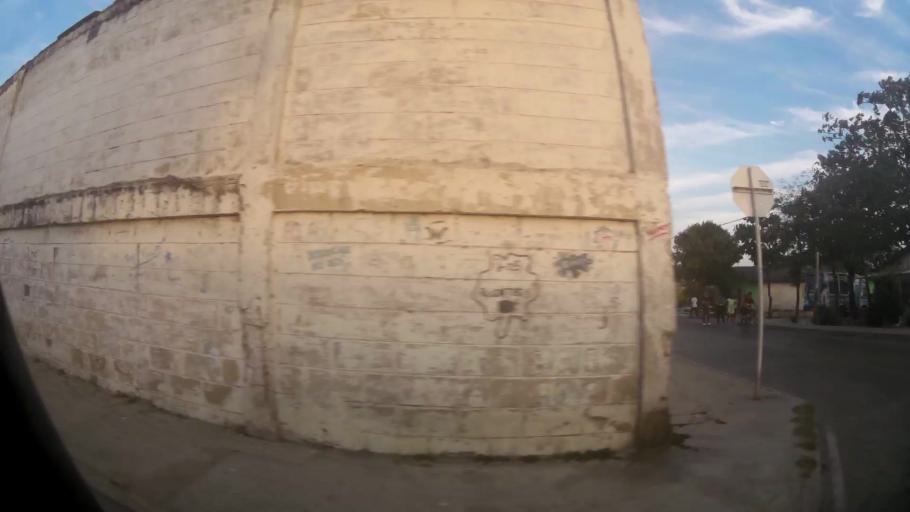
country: CO
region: Atlantico
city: Barranquilla
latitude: 10.9523
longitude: -74.8237
